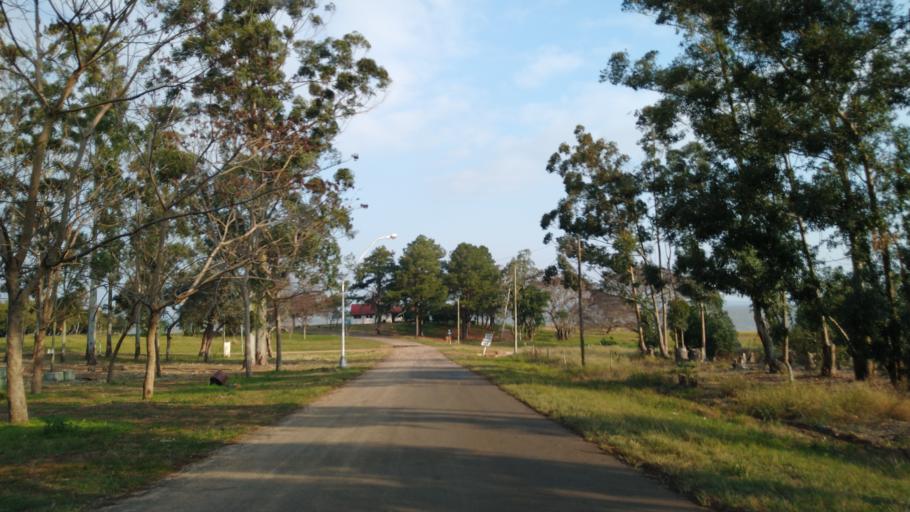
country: AR
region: Entre Rios
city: Santa Ana
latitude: -30.9131
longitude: -57.9269
